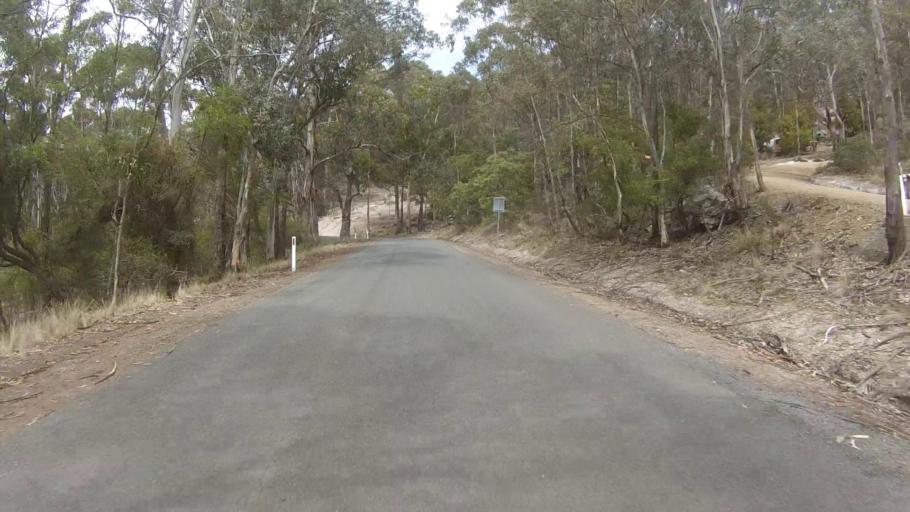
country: AU
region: Tasmania
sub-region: Kingborough
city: Blackmans Bay
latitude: -43.0483
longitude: 147.3387
